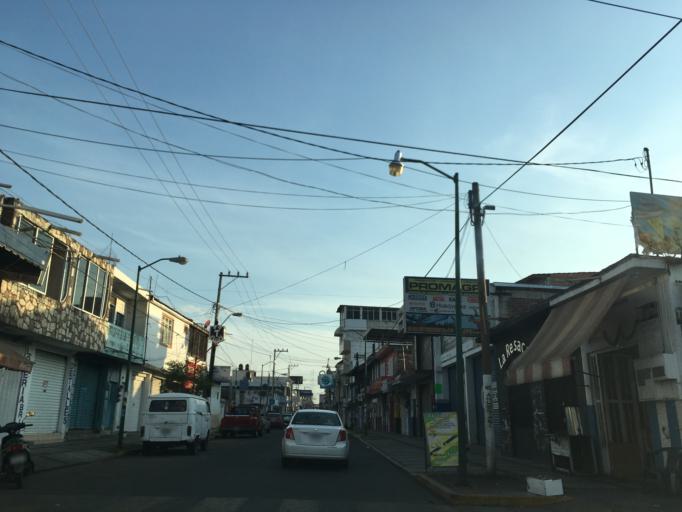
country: MX
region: Michoacan
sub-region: Los Reyes
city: La Higuerita (Colonia San Rafael)
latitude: 19.5933
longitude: -102.4730
